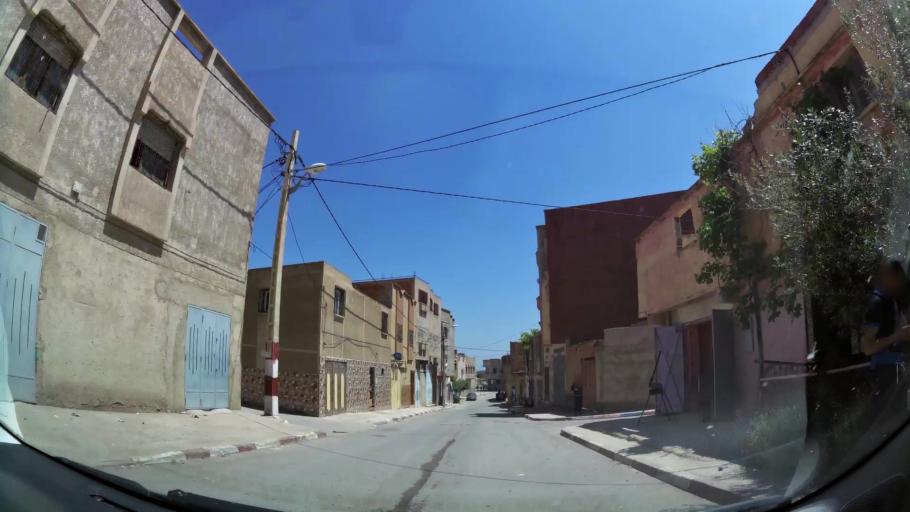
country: MA
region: Oriental
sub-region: Oujda-Angad
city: Oujda
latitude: 34.6805
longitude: -1.9514
